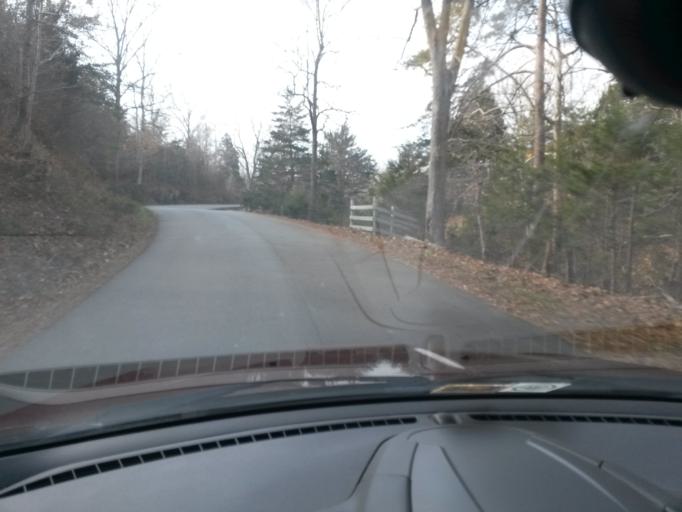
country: US
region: Virginia
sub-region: Botetourt County
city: Fincastle
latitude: 37.5846
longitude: -79.8704
